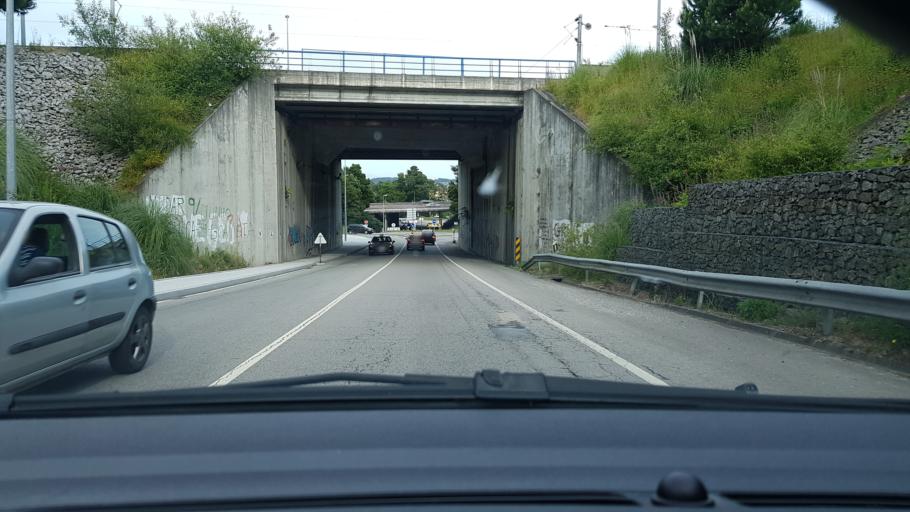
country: PT
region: Porto
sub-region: Maia
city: Leca do Bailio
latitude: 41.2103
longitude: -8.6299
